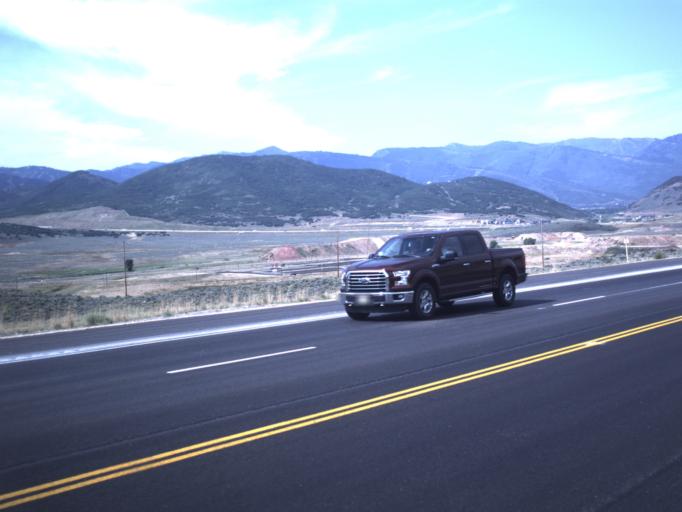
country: US
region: Utah
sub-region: Summit County
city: Park City
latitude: 40.6808
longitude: -111.4404
